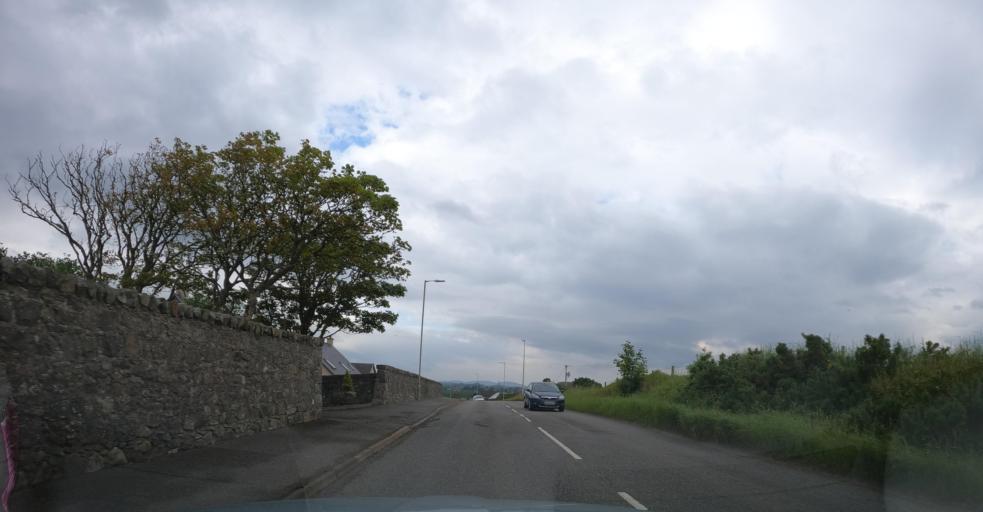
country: GB
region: Scotland
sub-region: Eilean Siar
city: Stornoway
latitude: 58.2077
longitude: -6.3606
